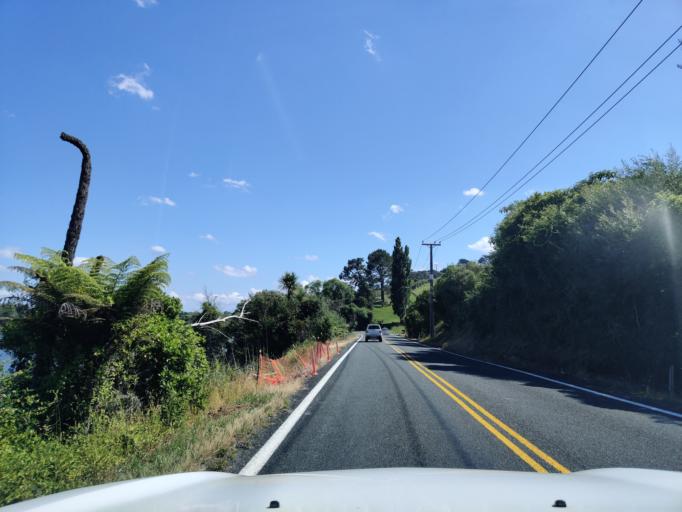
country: NZ
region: Waikato
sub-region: Waikato District
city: Ngaruawahia
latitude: -37.6534
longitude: 175.1433
